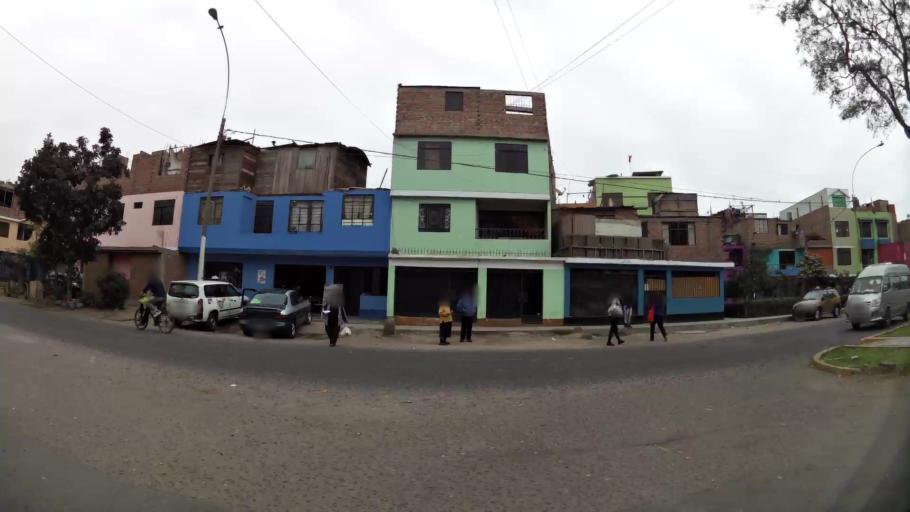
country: PE
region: Callao
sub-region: Callao
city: Callao
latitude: -12.0541
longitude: -77.1201
